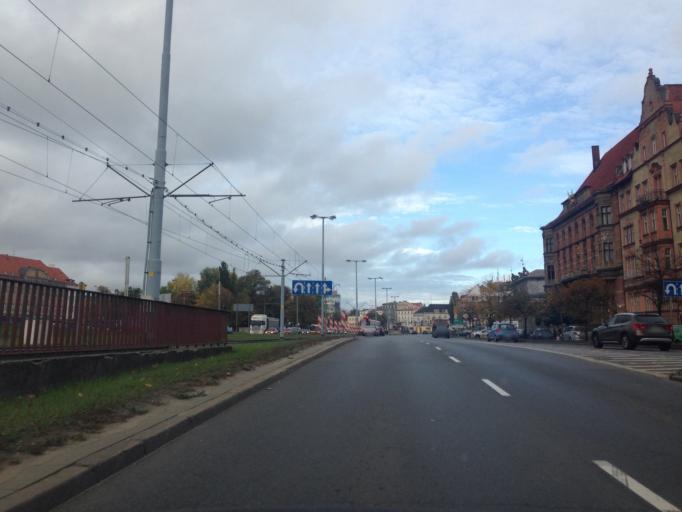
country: PL
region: Pomeranian Voivodeship
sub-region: Gdansk
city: Gdansk
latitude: 54.3487
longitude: 18.6457
